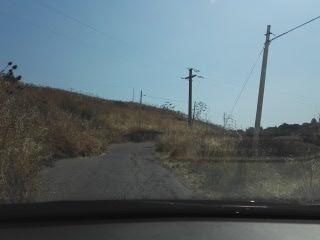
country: IT
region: Calabria
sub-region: Provincia di Reggio Calabria
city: Stignano
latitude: 38.4316
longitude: 16.4591
